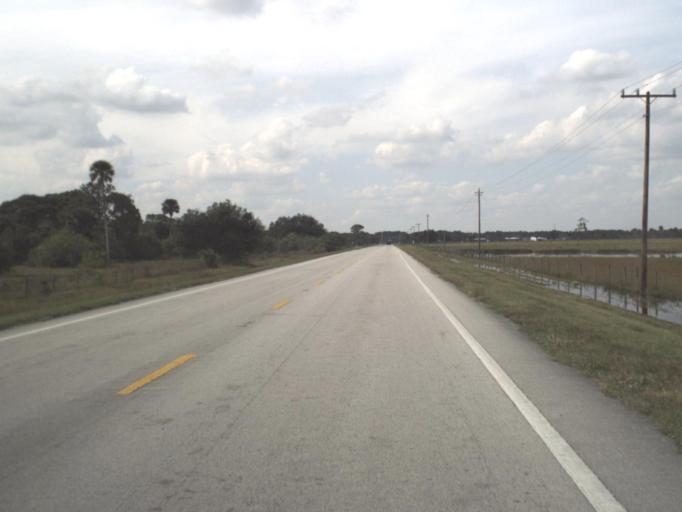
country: US
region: Florida
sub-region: Okeechobee County
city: Taylor Creek
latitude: 27.2230
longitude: -80.7668
